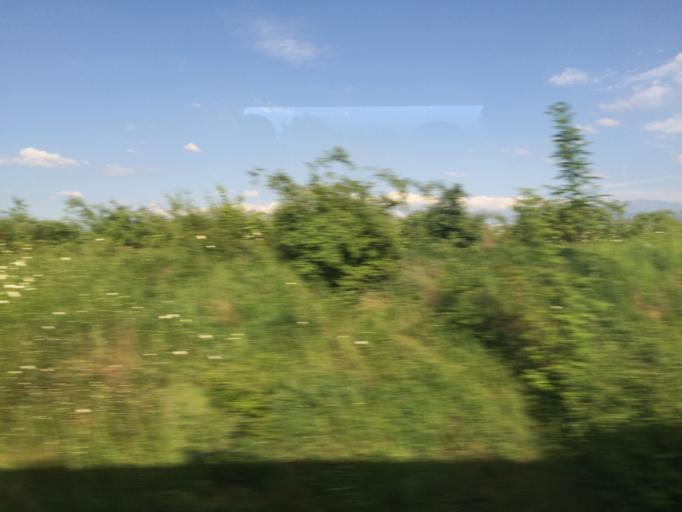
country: DE
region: North Rhine-Westphalia
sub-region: Regierungsbezirk Koln
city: Stossdorf
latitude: 50.7300
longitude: 7.2378
